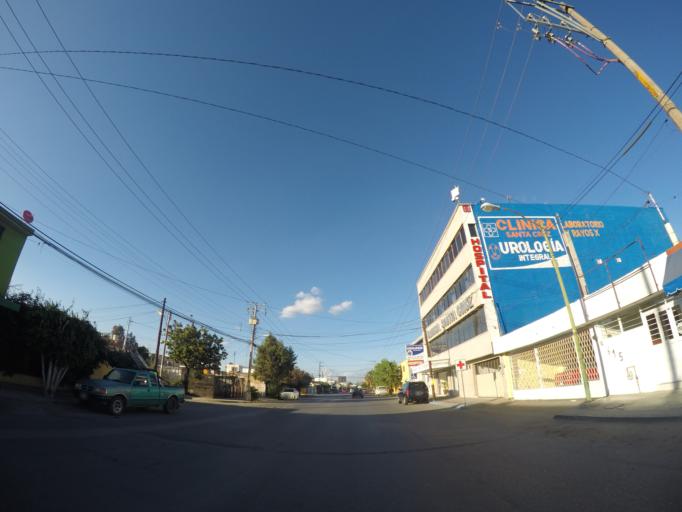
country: MX
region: San Luis Potosi
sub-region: San Luis Potosi
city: San Luis Potosi
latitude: 22.1742
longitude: -100.9990
